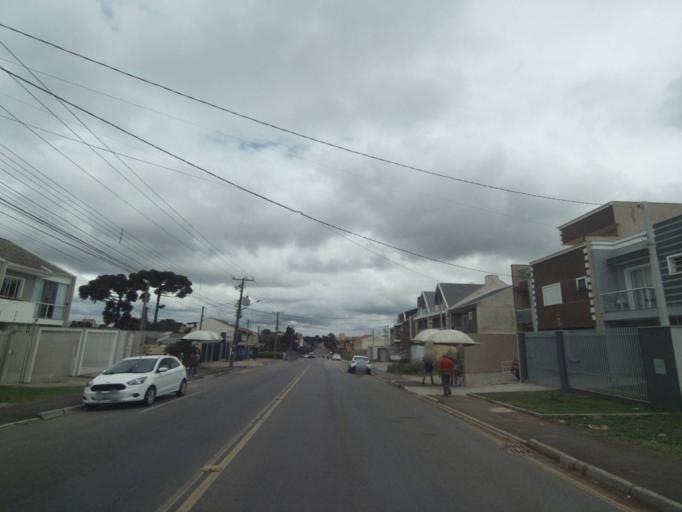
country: BR
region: Parana
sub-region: Curitiba
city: Curitiba
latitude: -25.4926
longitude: -49.3012
